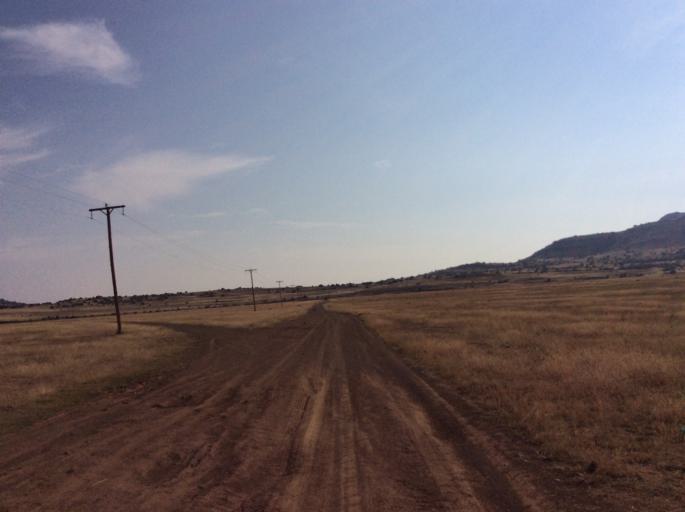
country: LS
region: Mafeteng
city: Mafeteng
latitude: -29.7094
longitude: 27.0089
